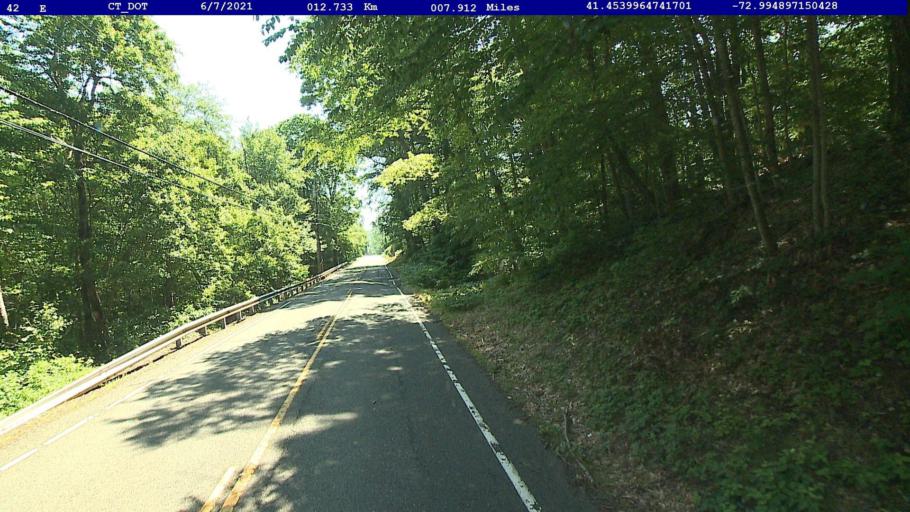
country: US
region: Connecticut
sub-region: New Haven County
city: Prospect
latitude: 41.4540
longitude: -72.9949
